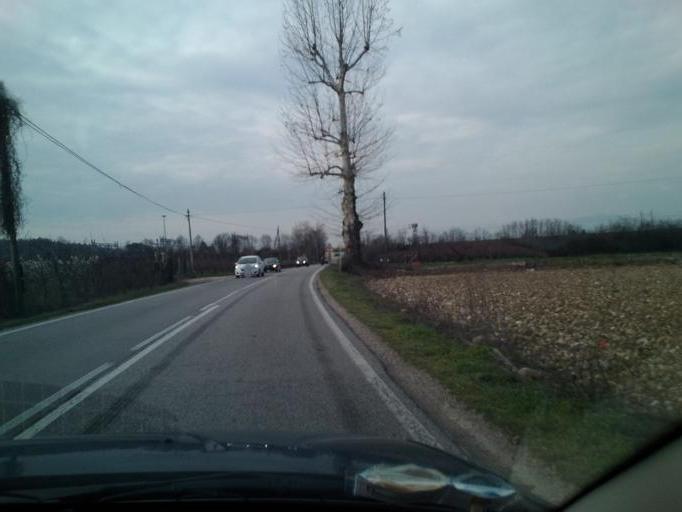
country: IT
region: Veneto
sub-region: Provincia di Verona
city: Sona
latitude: 45.4249
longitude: 10.8484
